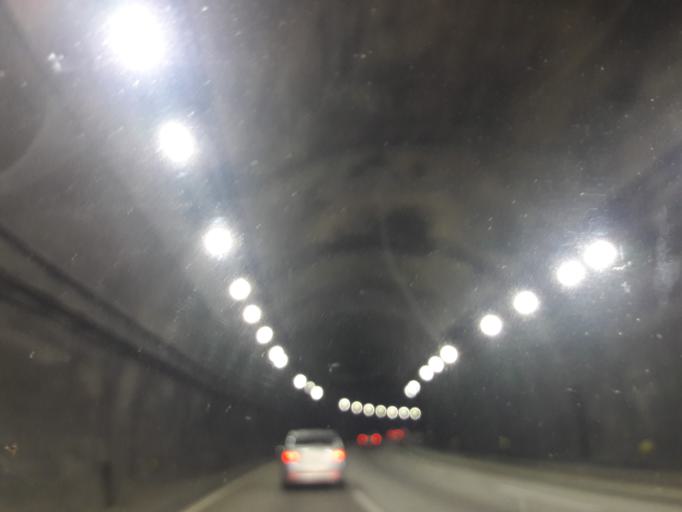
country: BR
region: Sao Paulo
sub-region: Cubatao
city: Cubatao
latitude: -23.9032
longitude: -46.5055
